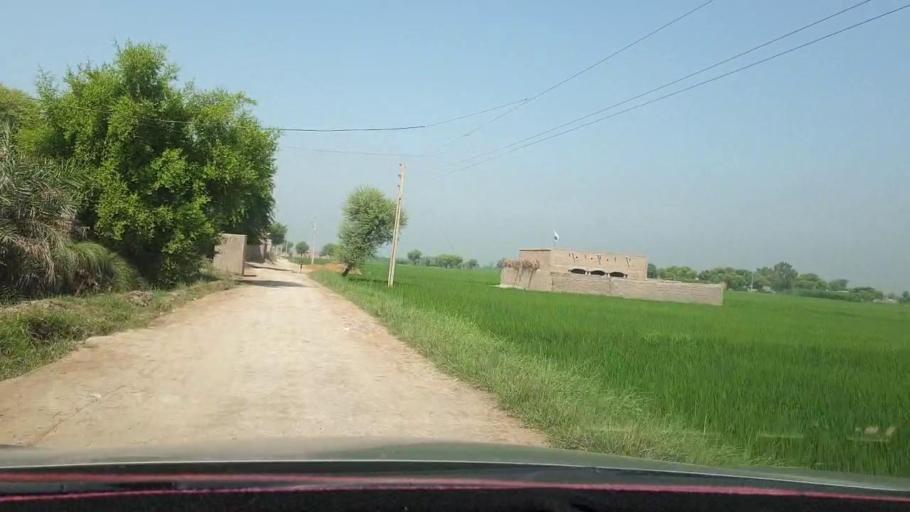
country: PK
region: Sindh
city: Kambar
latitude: 27.5809
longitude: 67.9372
